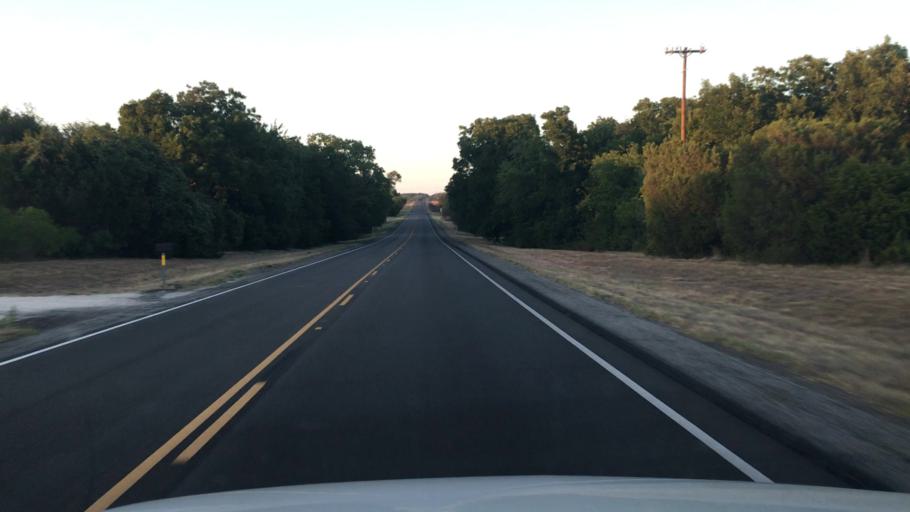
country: US
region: Texas
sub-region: Hamilton County
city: Hico
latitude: 32.0655
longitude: -97.9916
